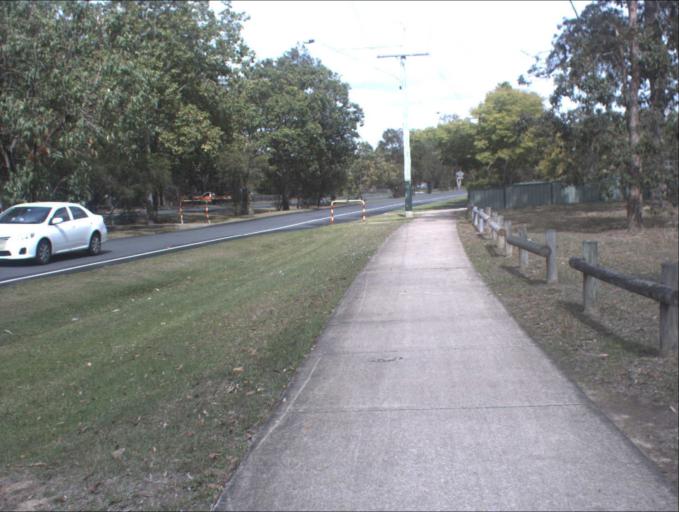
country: AU
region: Queensland
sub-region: Logan
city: Logan Reserve
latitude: -27.6783
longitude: 153.0684
